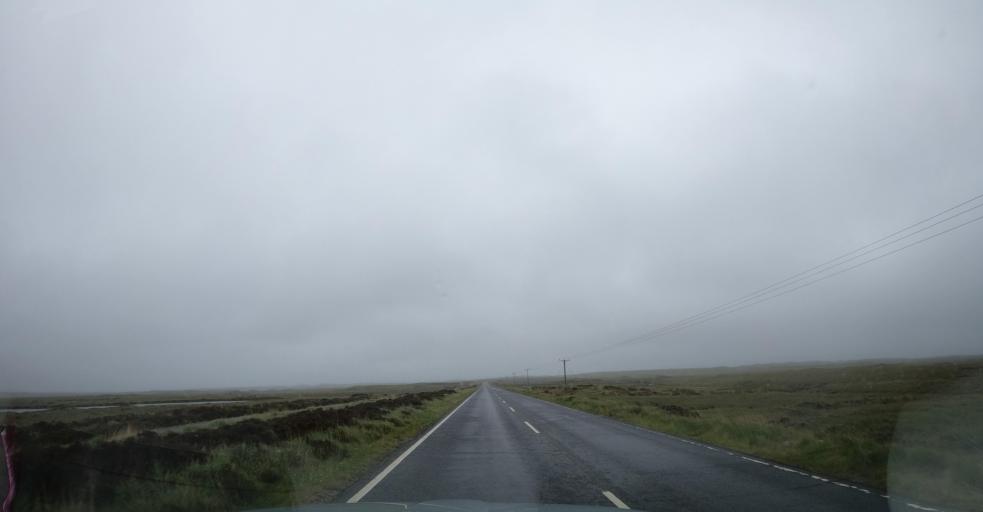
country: GB
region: Scotland
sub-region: Eilean Siar
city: Isle of North Uist
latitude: 57.5921
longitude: -7.2173
